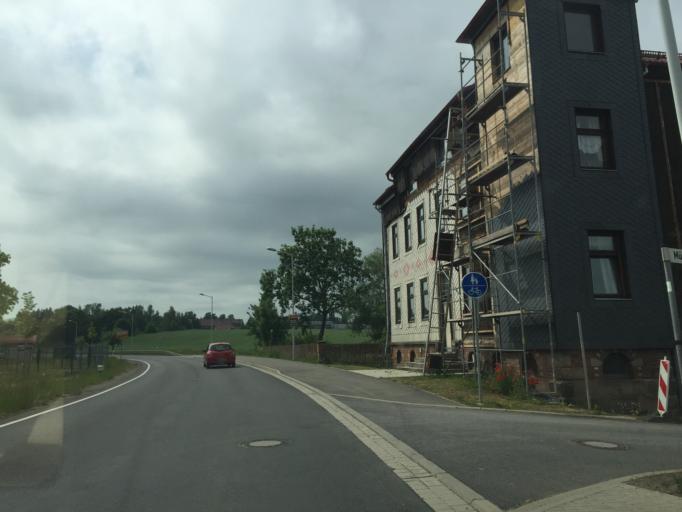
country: DE
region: Thuringia
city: Gehren
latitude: 50.6577
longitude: 11.0200
